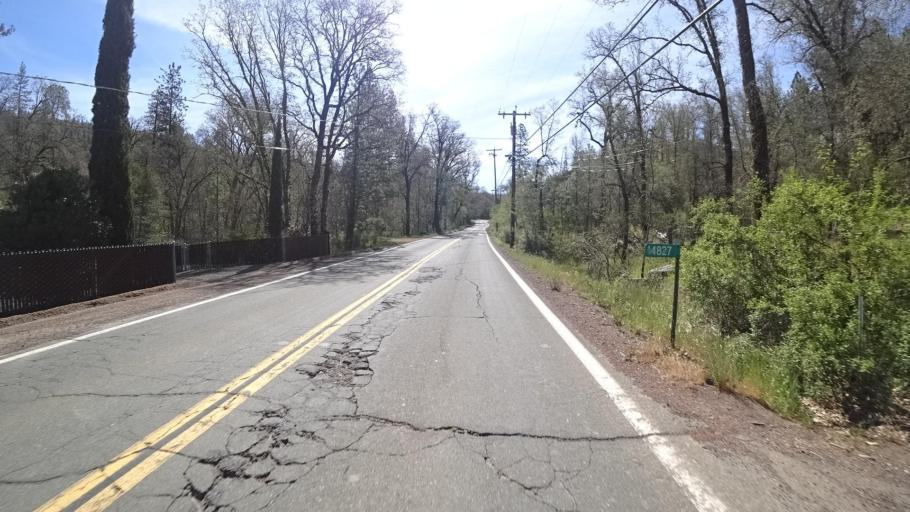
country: US
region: California
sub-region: Lake County
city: Cobb
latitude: 38.8459
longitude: -122.7528
